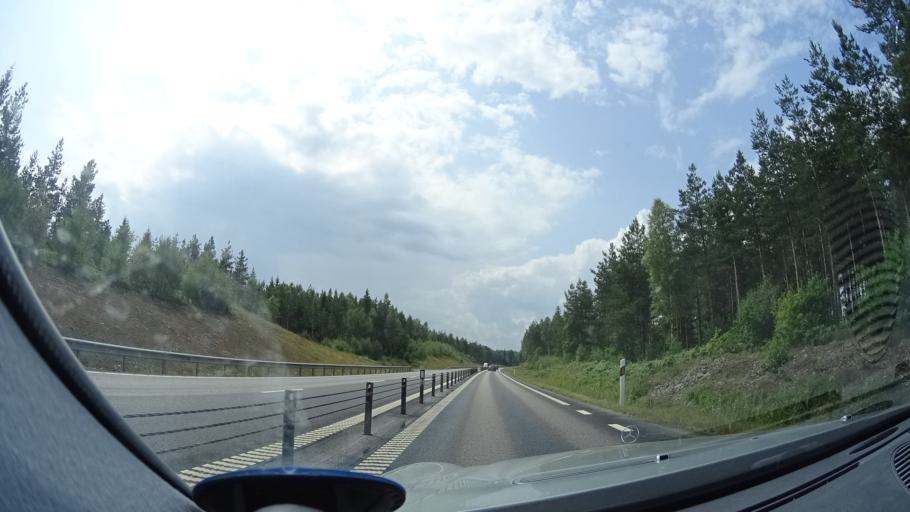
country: SE
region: Kalmar
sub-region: Nybro Kommun
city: Nybro
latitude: 56.7273
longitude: 15.8284
